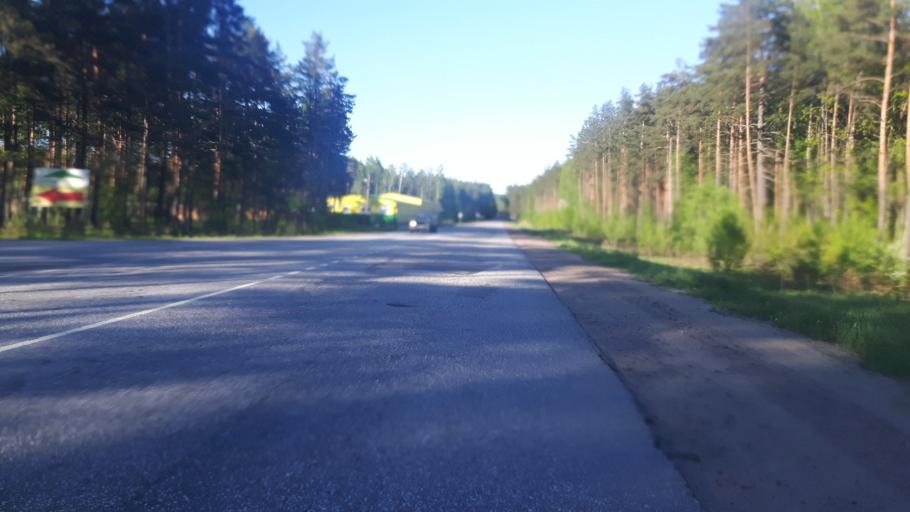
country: RU
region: Leningrad
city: Molodezhnoye
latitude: 60.1724
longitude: 29.4340
